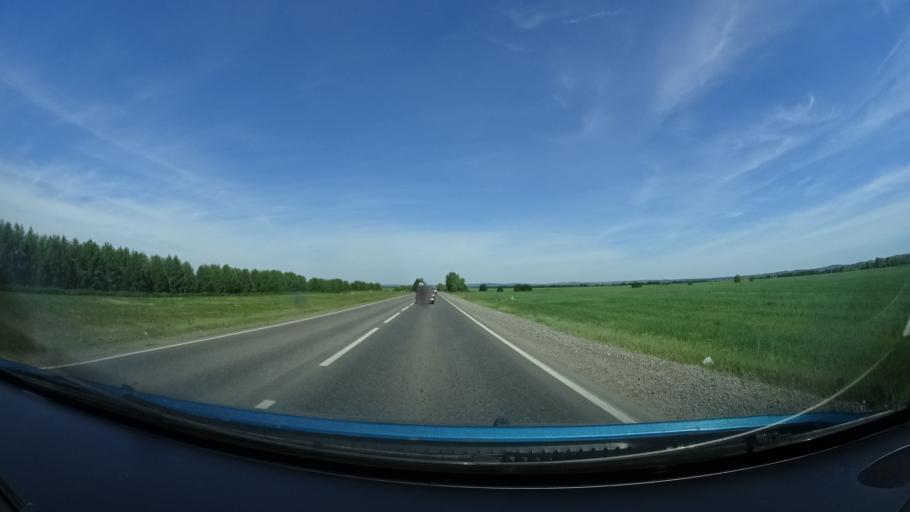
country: RU
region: Bashkortostan
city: Blagoveshchensk
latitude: 55.1887
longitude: 55.8433
